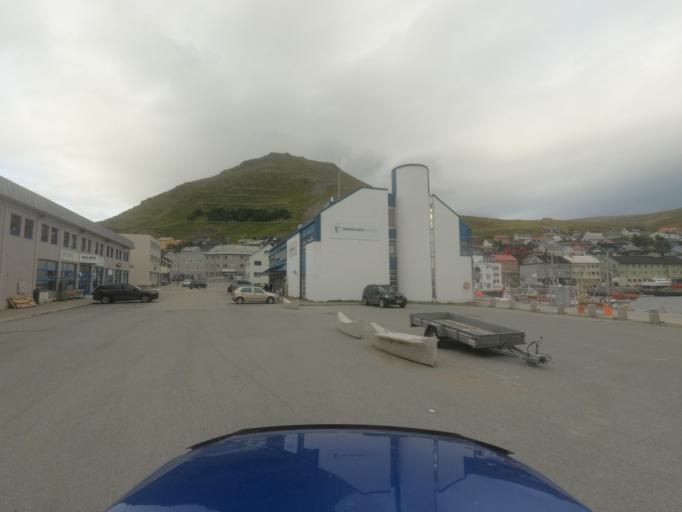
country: NO
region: Finnmark Fylke
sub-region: Nordkapp
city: Honningsvag
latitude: 70.9812
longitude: 25.9694
